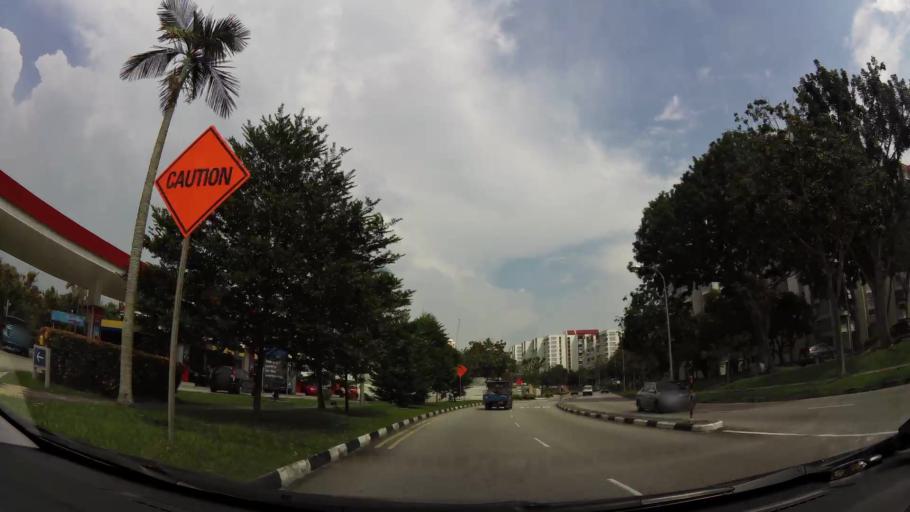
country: SG
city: Singapore
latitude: 1.3604
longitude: 103.9475
